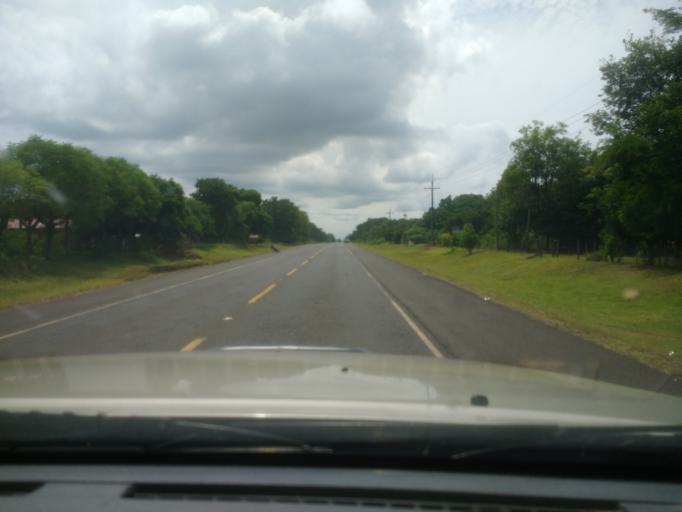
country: PY
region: San Pedro
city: Puerto Rosario
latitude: -24.4348
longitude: -57.0195
